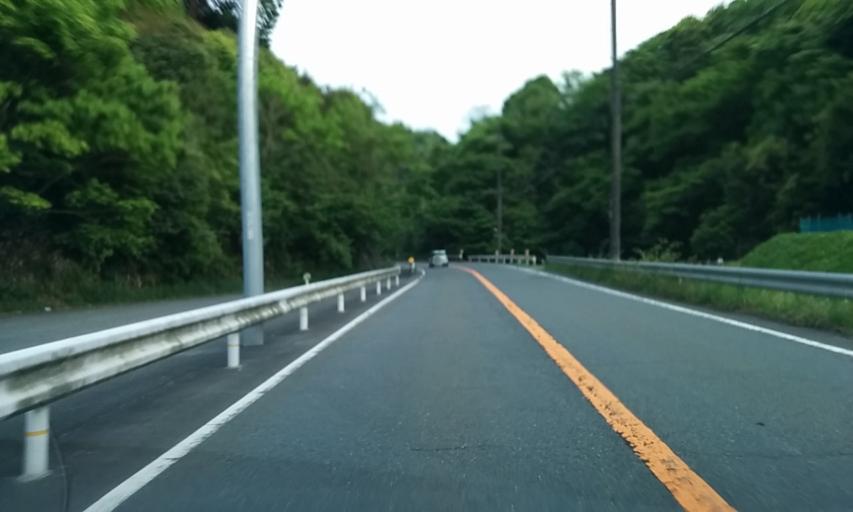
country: JP
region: Kyoto
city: Ayabe
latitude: 35.2296
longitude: 135.3348
